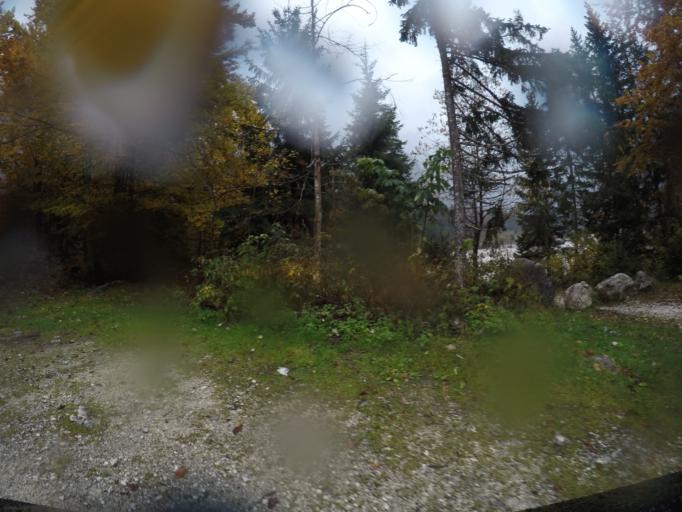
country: SI
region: Kranjska Gora
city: Kranjska Gora
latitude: 46.4042
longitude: 13.7100
